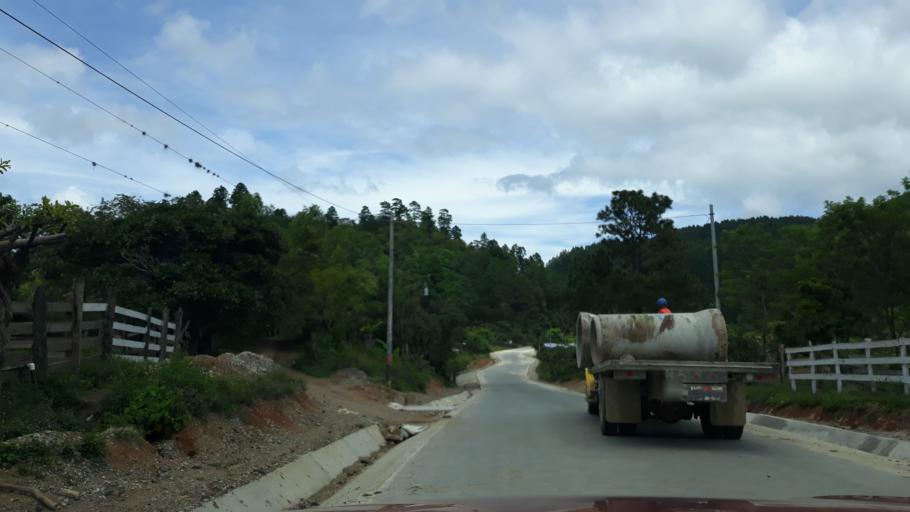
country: HN
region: El Paraiso
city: Santa Cruz
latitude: 13.7407
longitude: -86.6265
